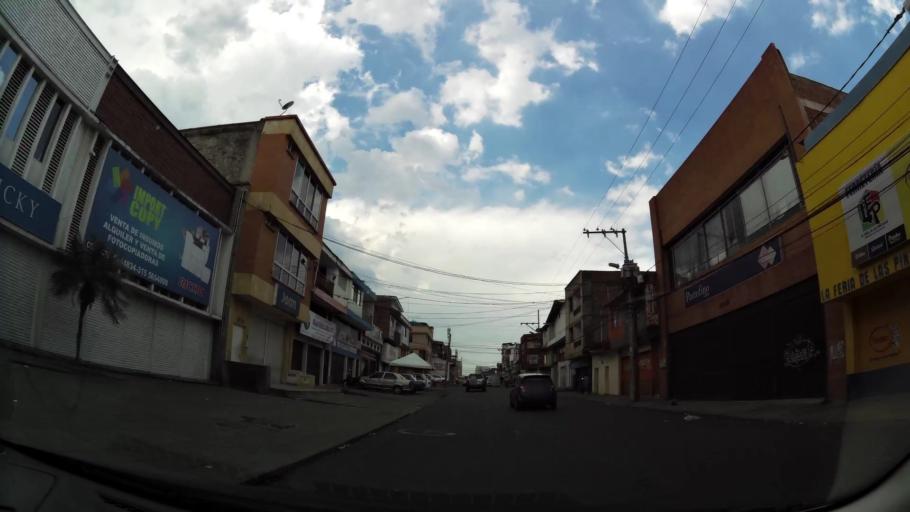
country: CO
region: Valle del Cauca
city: Cali
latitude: 3.4357
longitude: -76.5346
